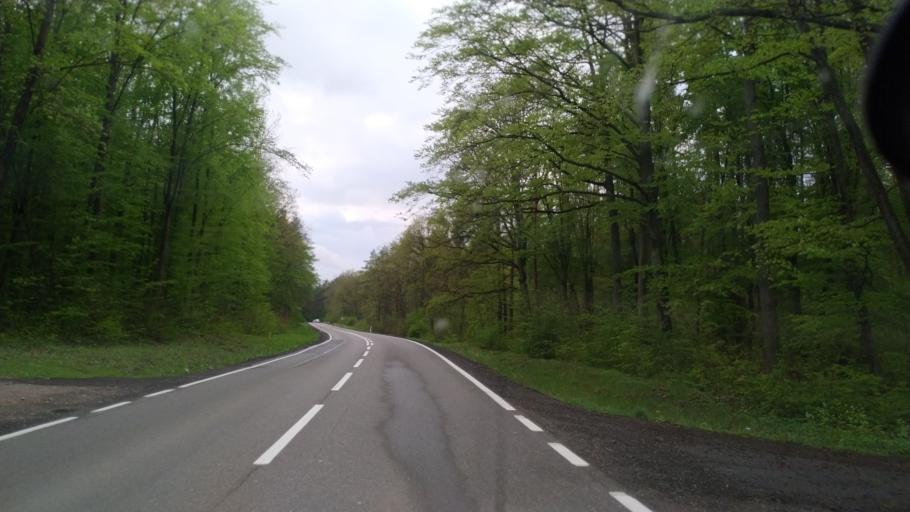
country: PL
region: Pomeranian Voivodeship
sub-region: Powiat kwidzynski
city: Ryjewo
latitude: 53.8107
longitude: 18.9696
